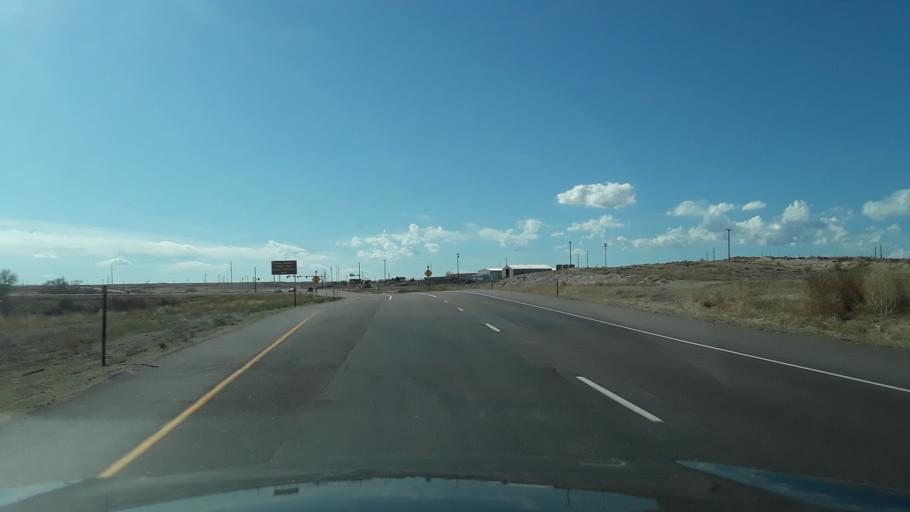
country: US
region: Colorado
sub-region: Pueblo County
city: Pueblo West
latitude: 38.3143
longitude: -104.6570
